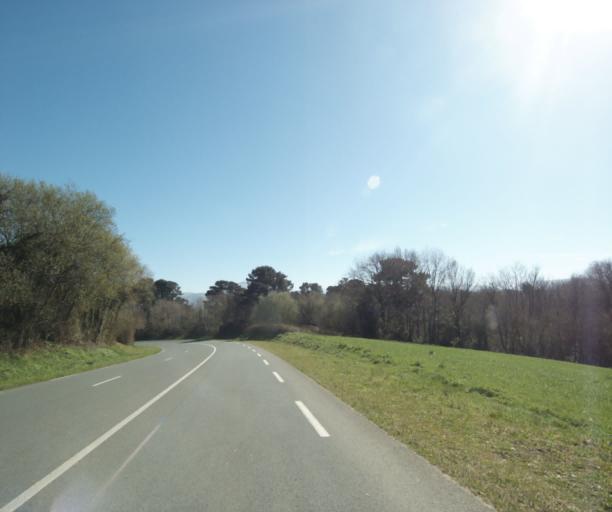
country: FR
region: Aquitaine
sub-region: Departement des Pyrenees-Atlantiques
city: Urrugne
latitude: 43.3856
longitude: -1.6988
